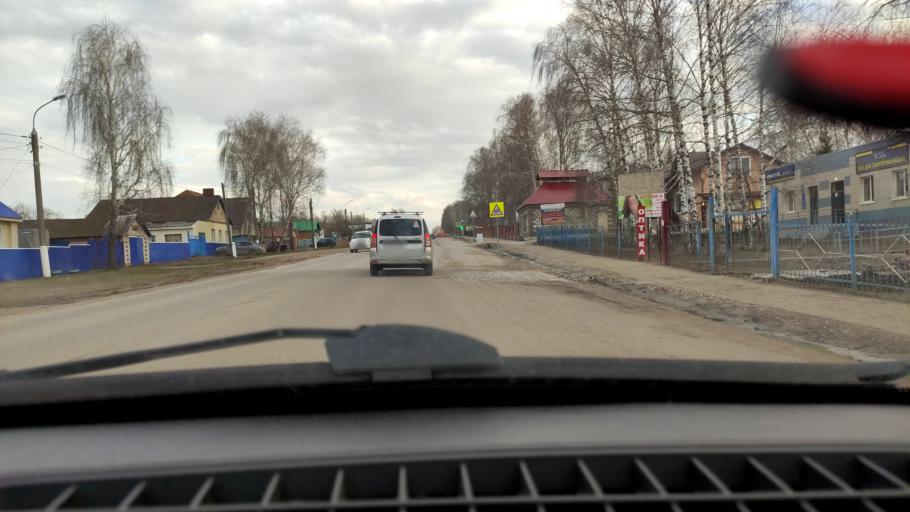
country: RU
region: Bashkortostan
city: Tolbazy
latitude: 54.0199
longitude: 55.8864
